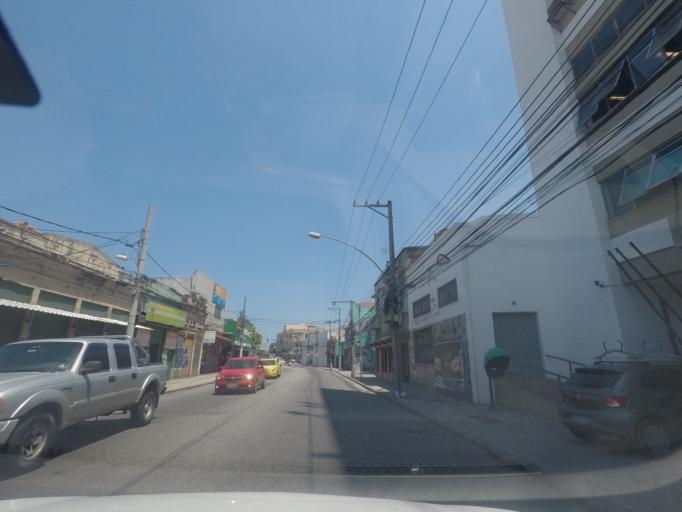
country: BR
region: Rio de Janeiro
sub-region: Rio De Janeiro
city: Rio de Janeiro
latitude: -22.8534
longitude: -43.2623
